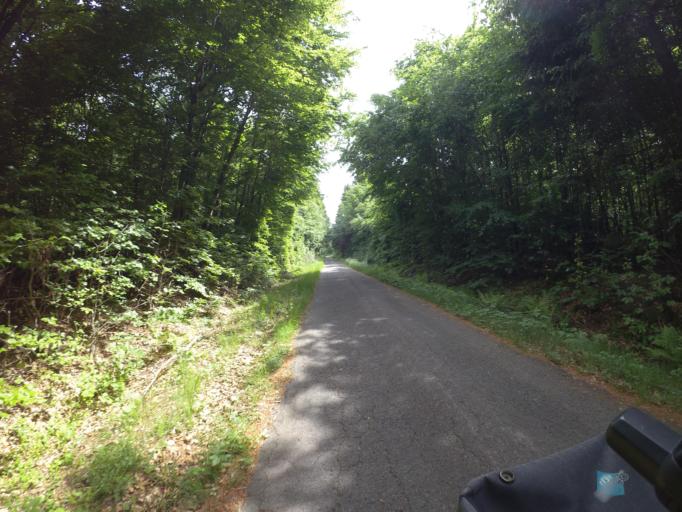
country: DE
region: Rheinland-Pfalz
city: Damflos
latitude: 49.6818
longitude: 7.0042
